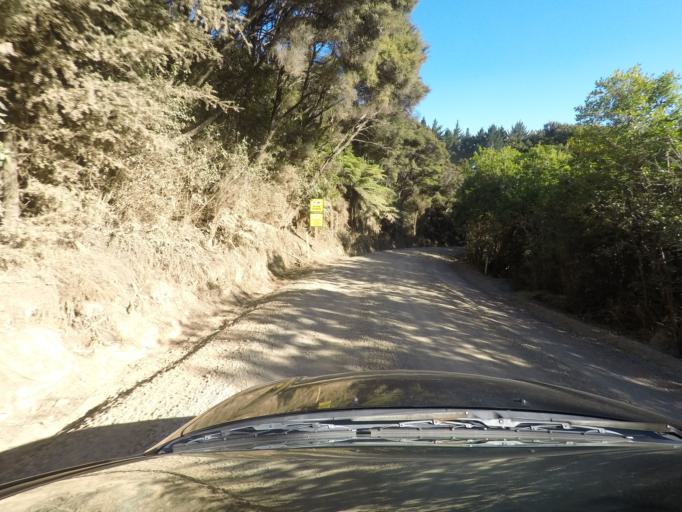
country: NZ
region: Northland
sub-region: Far North District
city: Paihia
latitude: -35.2558
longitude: 174.0708
